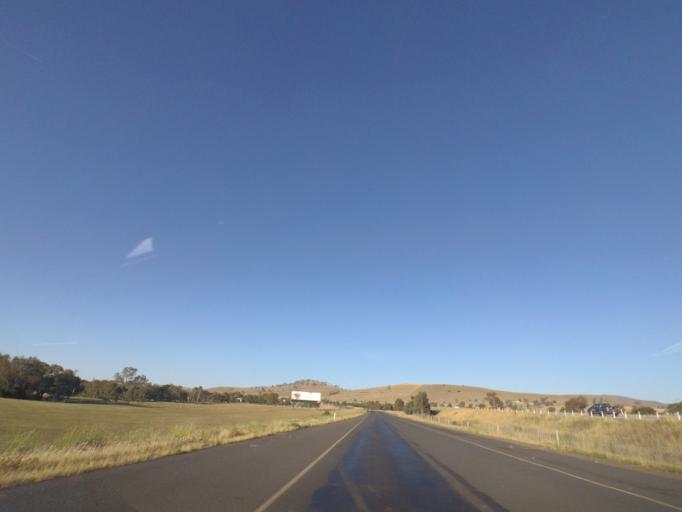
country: AU
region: New South Wales
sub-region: Gundagai
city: Gundagai
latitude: -34.9514
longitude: 148.1640
